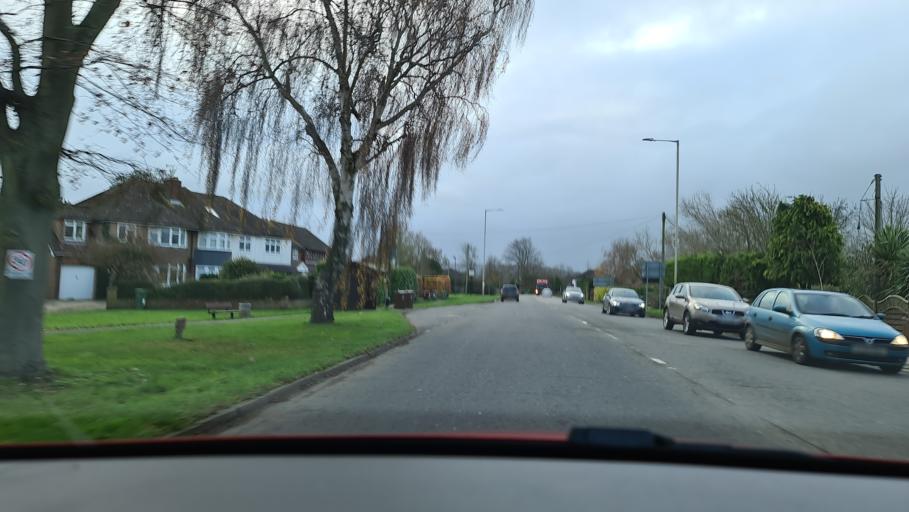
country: GB
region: England
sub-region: Buckinghamshire
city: Weston Turville
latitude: 51.7856
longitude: -0.7910
